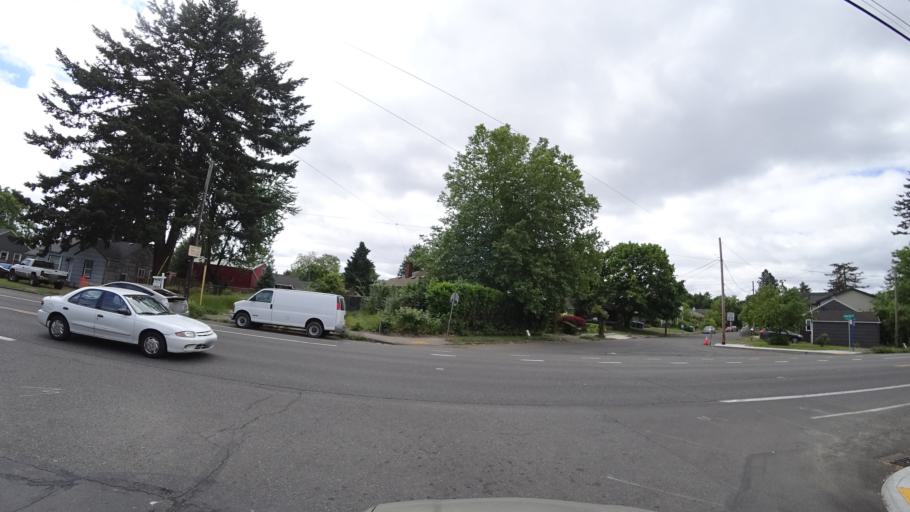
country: US
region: Oregon
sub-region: Washington County
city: West Haven
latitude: 45.5959
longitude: -122.7517
